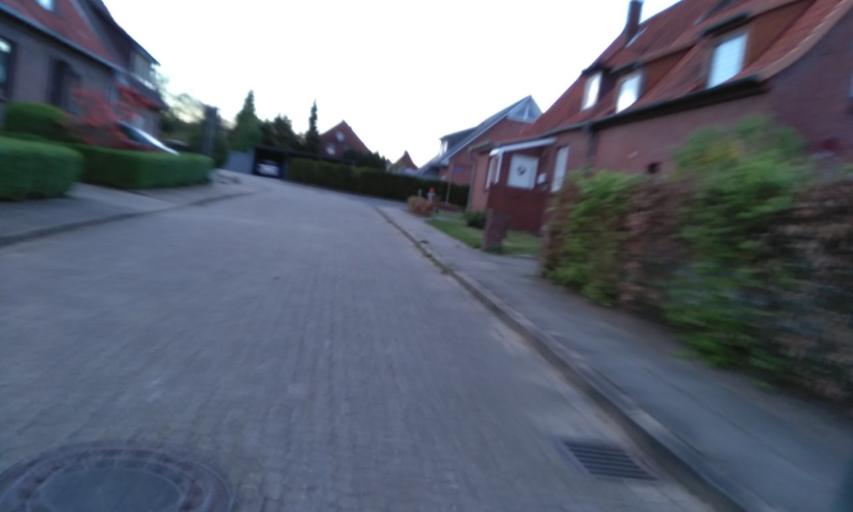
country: DE
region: Lower Saxony
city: Horneburg
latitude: 53.5080
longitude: 9.5703
